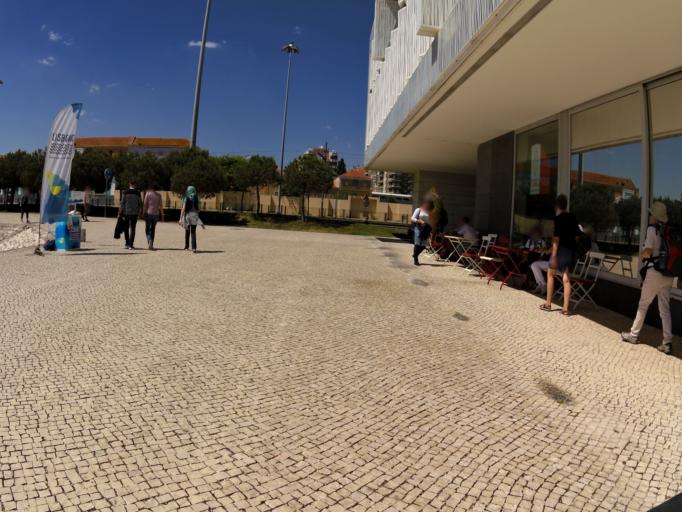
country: PT
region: Lisbon
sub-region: Oeiras
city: Alges
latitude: 38.6936
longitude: -9.2109
